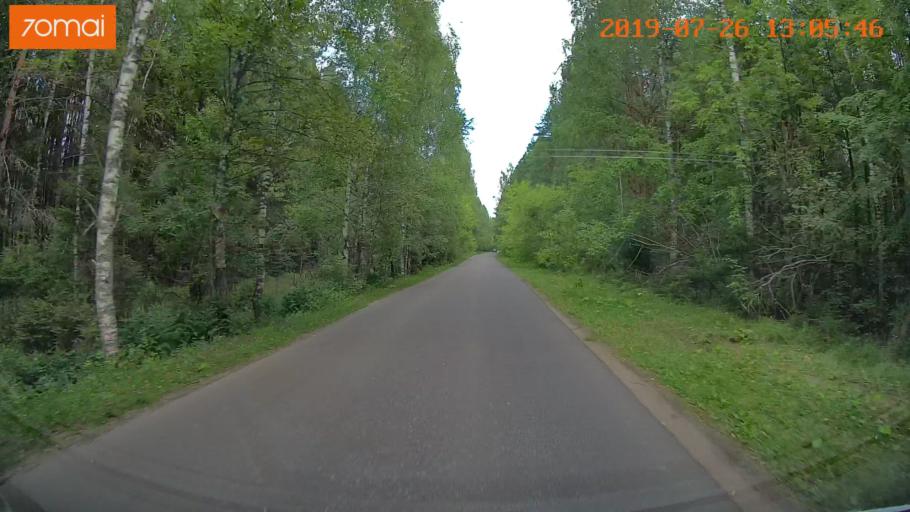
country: RU
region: Ivanovo
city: Bogorodskoye
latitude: 57.0653
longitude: 41.0390
